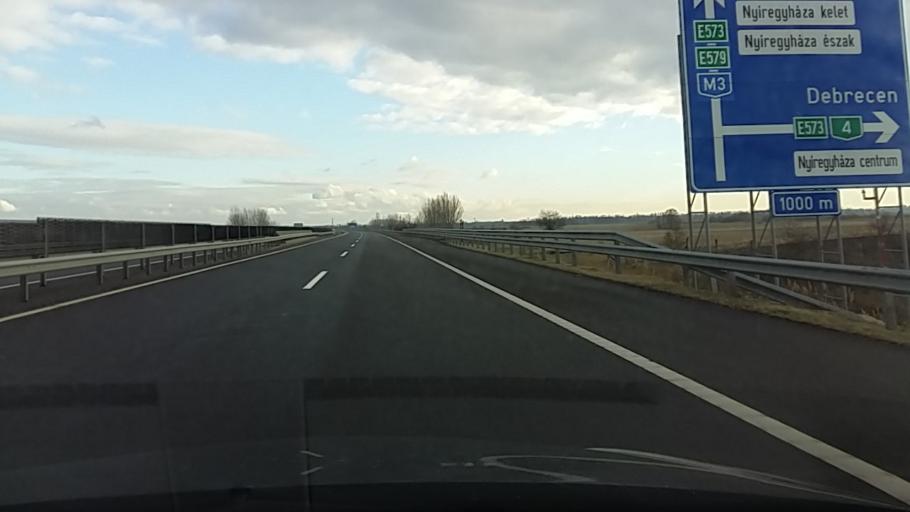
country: HU
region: Szabolcs-Szatmar-Bereg
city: Nyiregyhaza
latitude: 47.8891
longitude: 21.6938
